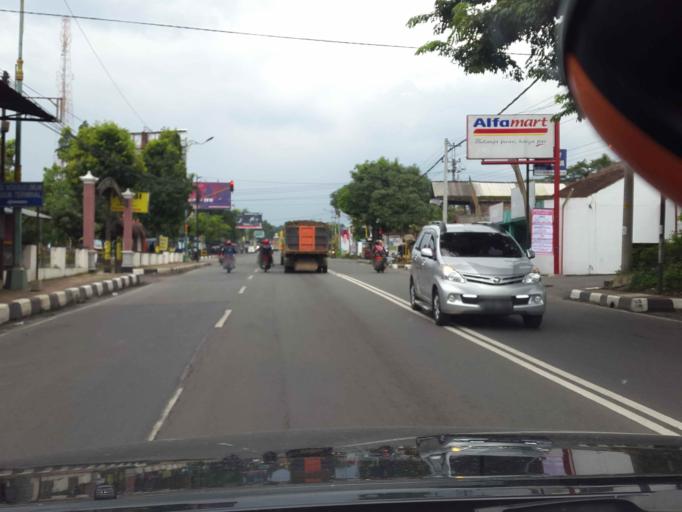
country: ID
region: Central Java
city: Salatiga
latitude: -7.3607
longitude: 110.5135
